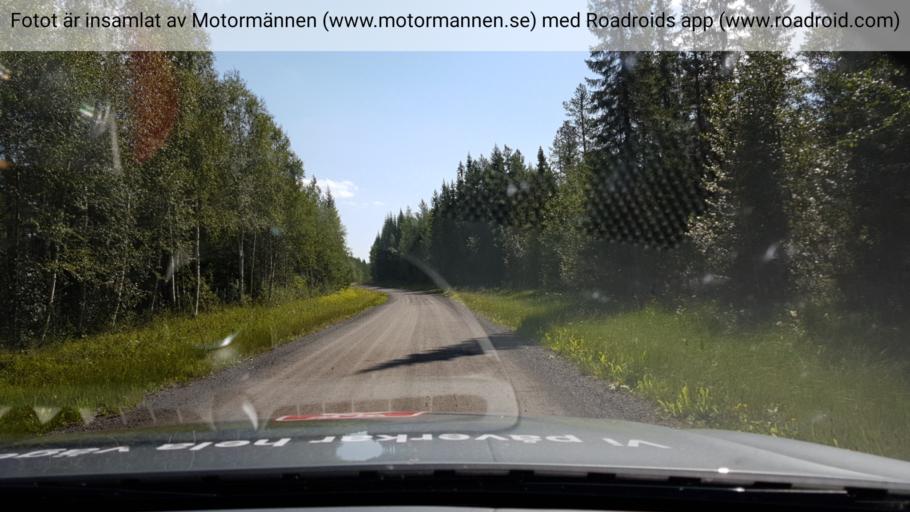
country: SE
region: Jaemtland
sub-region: Stroemsunds Kommun
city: Stroemsund
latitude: 63.3439
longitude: 15.3915
